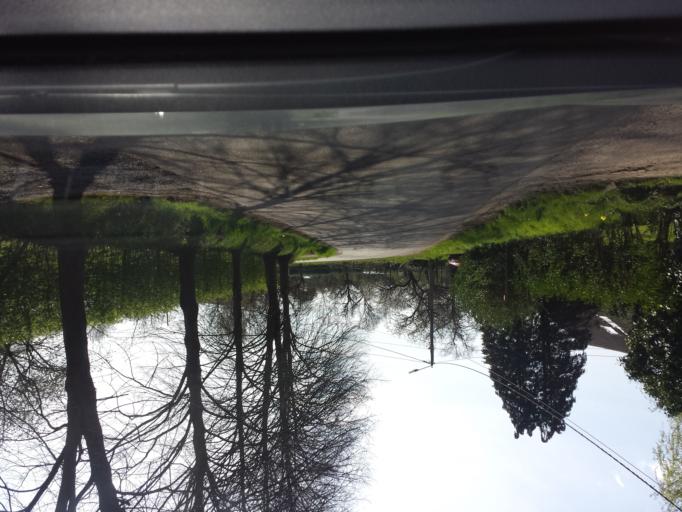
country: BE
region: Flanders
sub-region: Provincie Limburg
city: Lummen
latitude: 51.0168
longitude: 5.1681
